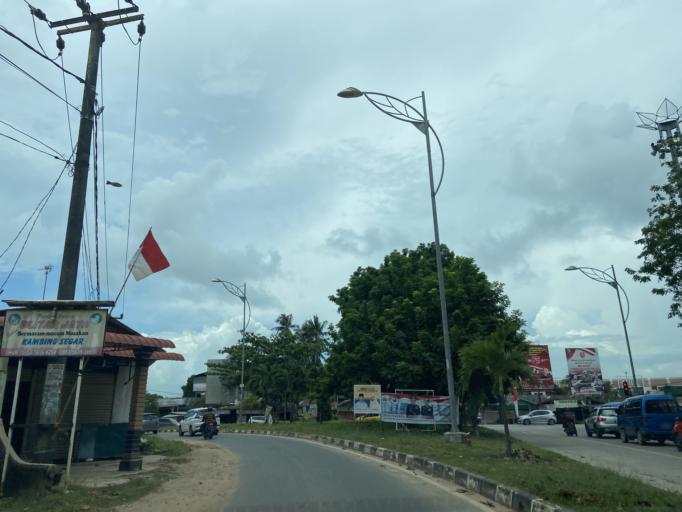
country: SG
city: Singapore
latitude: 1.1489
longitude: 104.1321
